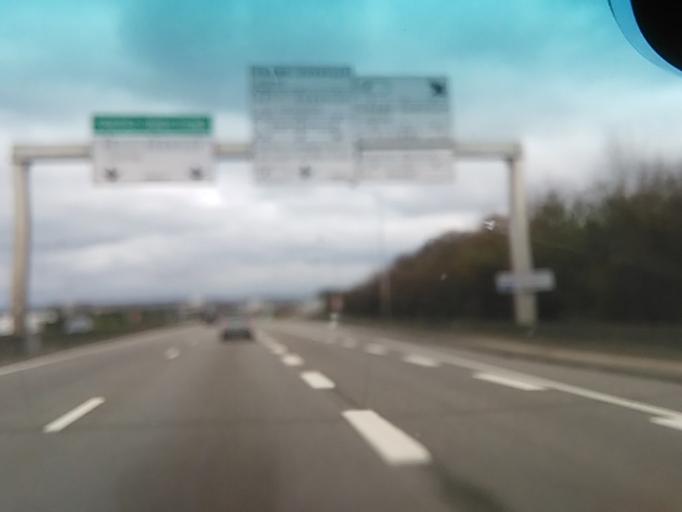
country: FR
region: Haute-Normandie
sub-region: Departement de la Seine-Maritime
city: Le Grand-Quevilly
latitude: 49.4056
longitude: 1.0356
